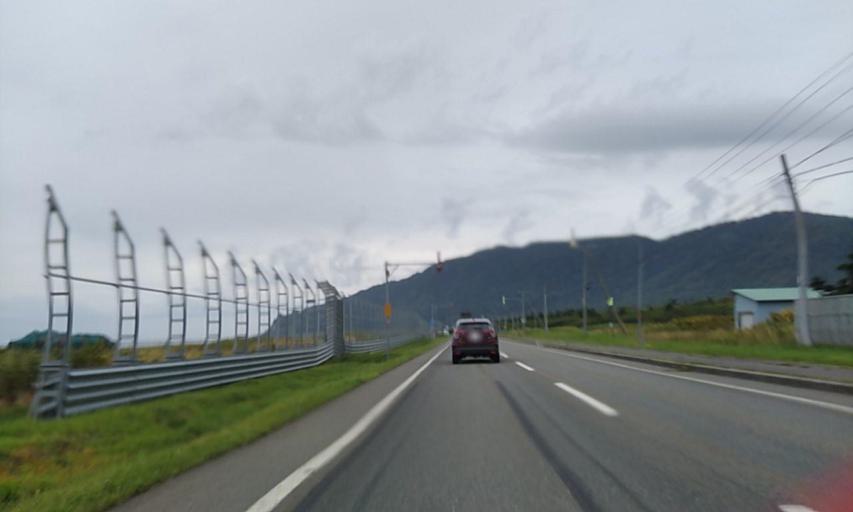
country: JP
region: Hokkaido
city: Makubetsu
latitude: 45.0776
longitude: 142.4604
